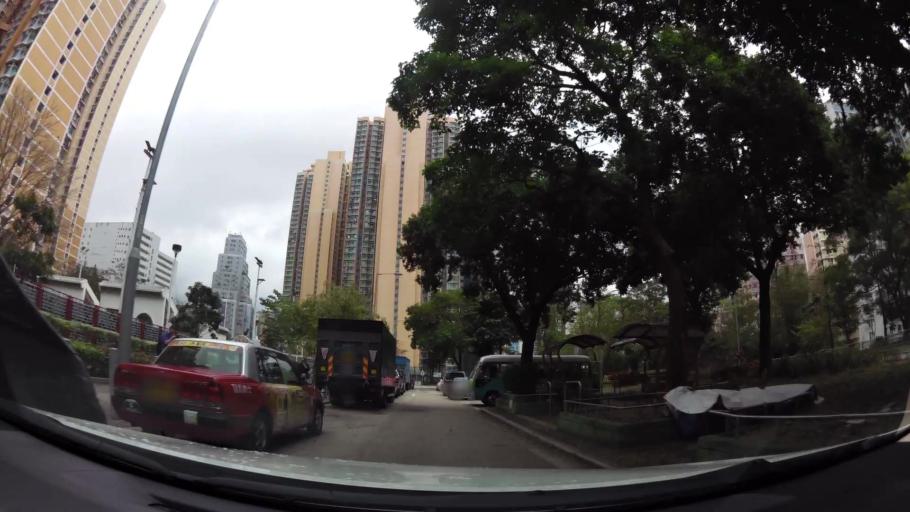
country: HK
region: Tsuen Wan
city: Tsuen Wan
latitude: 22.3667
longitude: 114.1312
